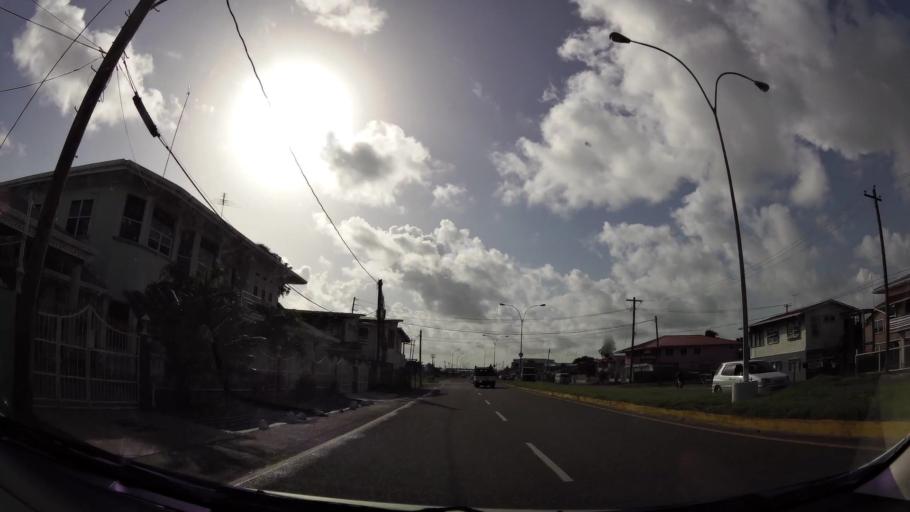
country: GY
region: Demerara-Mahaica
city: Georgetown
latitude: 6.8192
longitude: -58.0909
